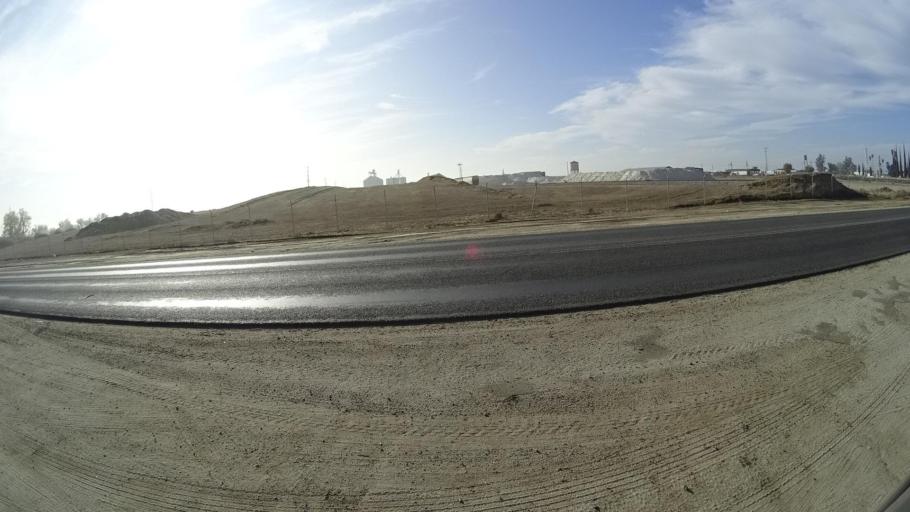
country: US
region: California
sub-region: Kern County
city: McFarland
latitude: 35.6022
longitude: -119.2067
